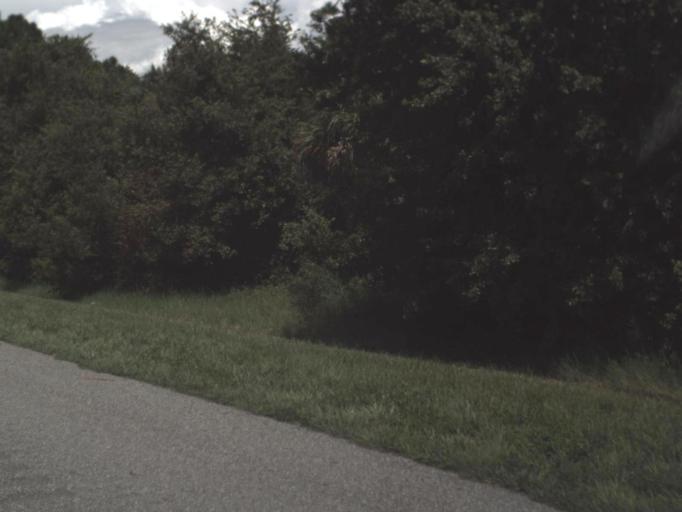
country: US
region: Florida
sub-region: Hillsborough County
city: Progress Village
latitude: 27.8834
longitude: -82.3481
